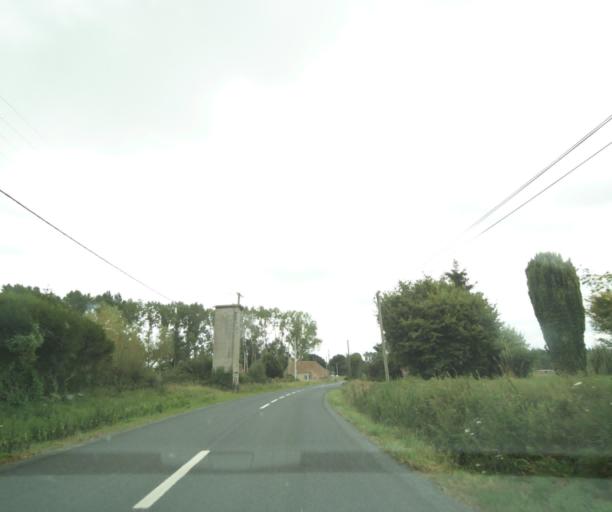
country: FR
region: Pays de la Loire
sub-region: Departement de Maine-et-Loire
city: Durtal
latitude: 47.7181
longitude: -0.2629
